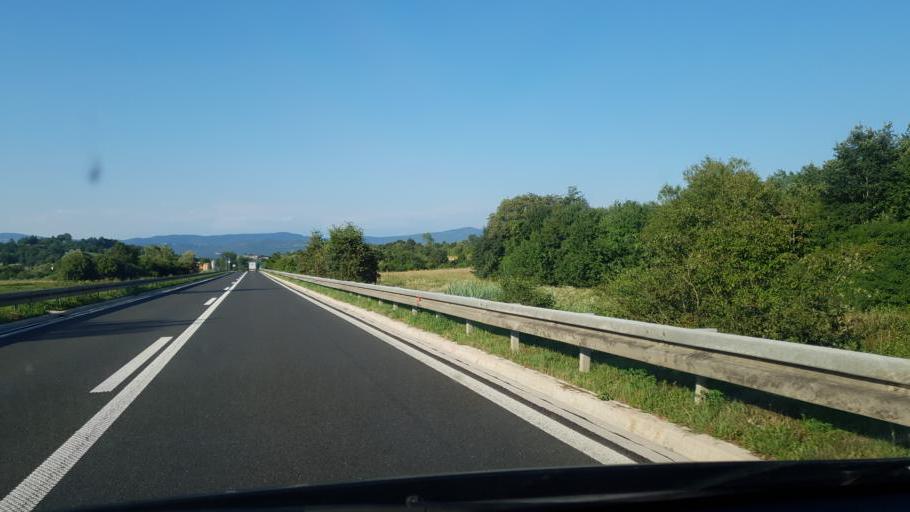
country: HR
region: Istarska
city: Pazin
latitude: 45.2983
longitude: 14.0475
